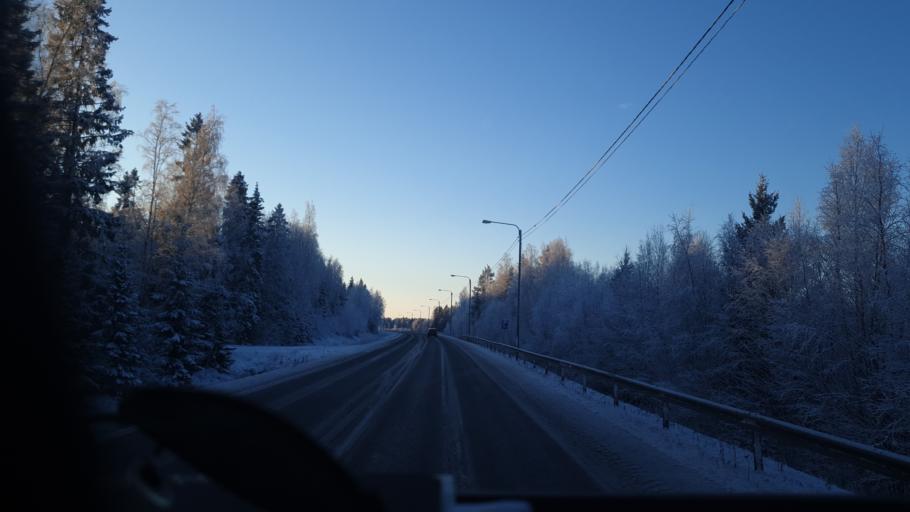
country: FI
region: Central Ostrobothnia
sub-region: Kokkola
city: Kaelviae
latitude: 63.9221
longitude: 23.4149
